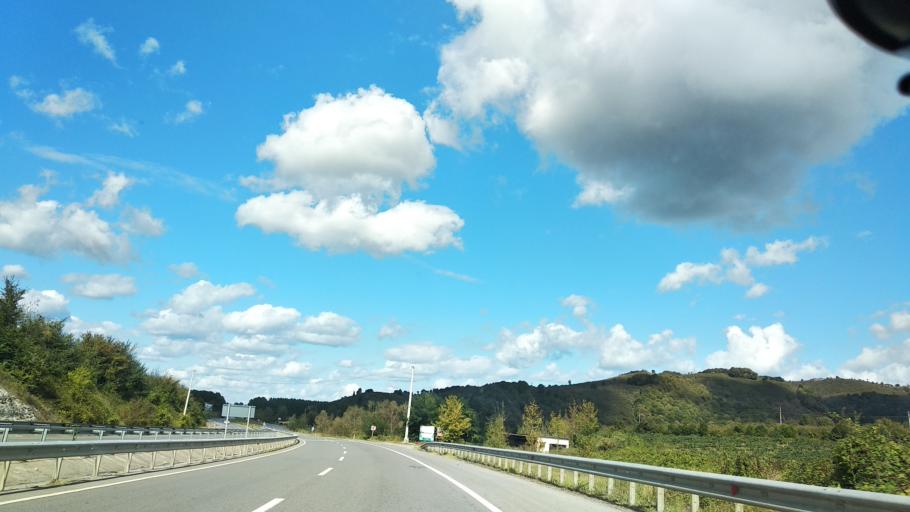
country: TR
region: Sakarya
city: Karasu
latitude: 41.0506
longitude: 30.6342
